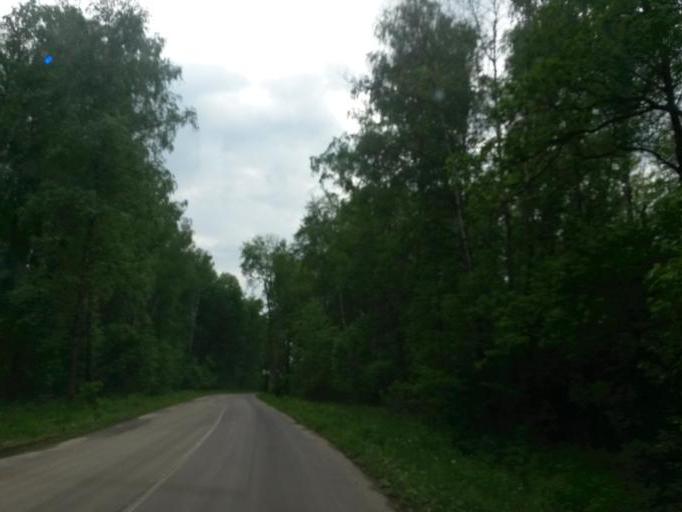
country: RU
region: Moskovskaya
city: Melikhovo
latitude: 55.1587
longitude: 37.6693
